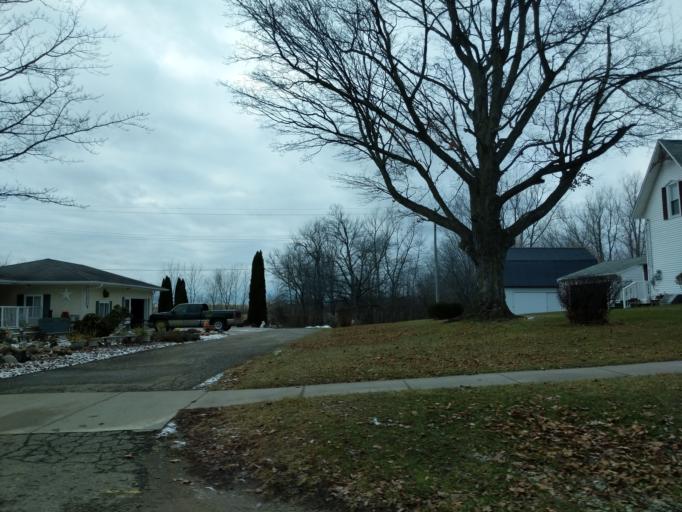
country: US
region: Michigan
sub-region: Lapeer County
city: North Branch
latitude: 43.3185
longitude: -83.1793
